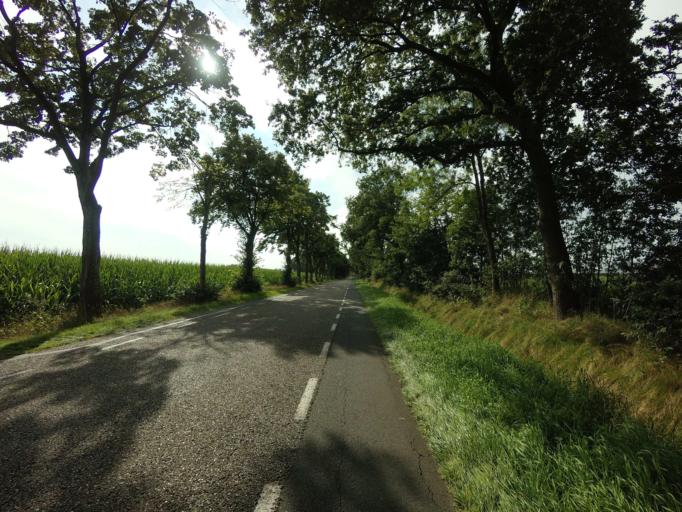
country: NL
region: Drenthe
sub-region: Gemeente Coevorden
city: Coevorden
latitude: 52.6920
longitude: 6.7159
